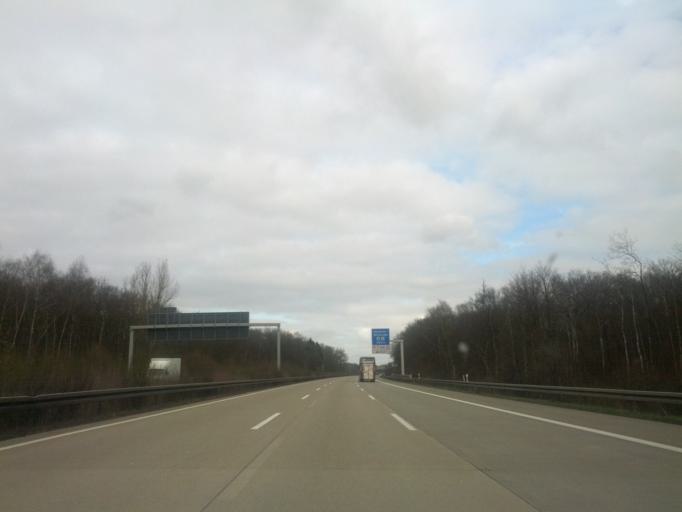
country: DE
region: Lower Saxony
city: Laatzen
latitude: 52.3170
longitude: 9.8657
